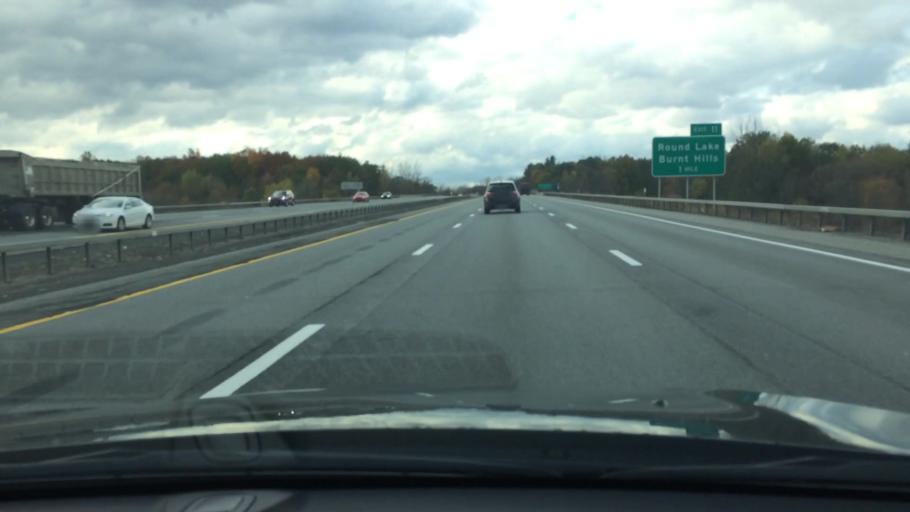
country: US
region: New York
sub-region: Saratoga County
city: Country Knolls
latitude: 42.9534
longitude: -73.8033
